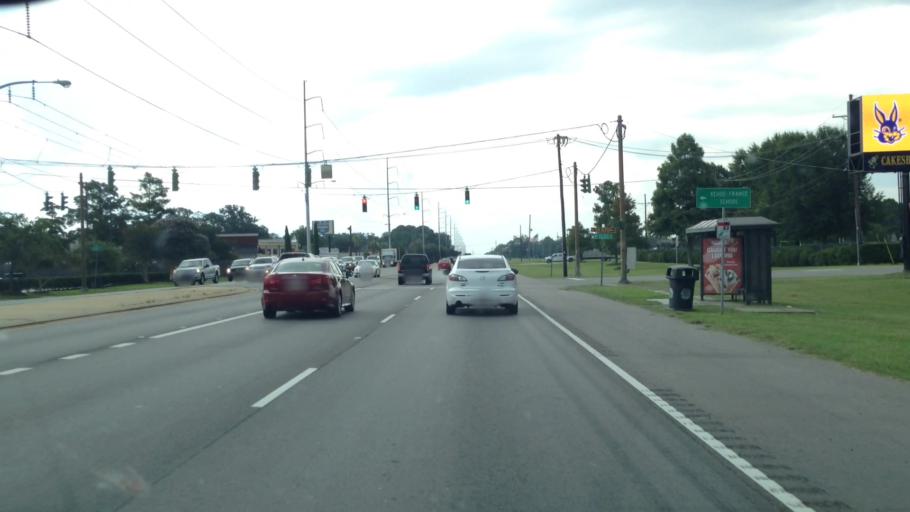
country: US
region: Louisiana
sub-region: Jefferson Parish
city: Elmwood
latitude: 29.9767
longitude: -90.1968
